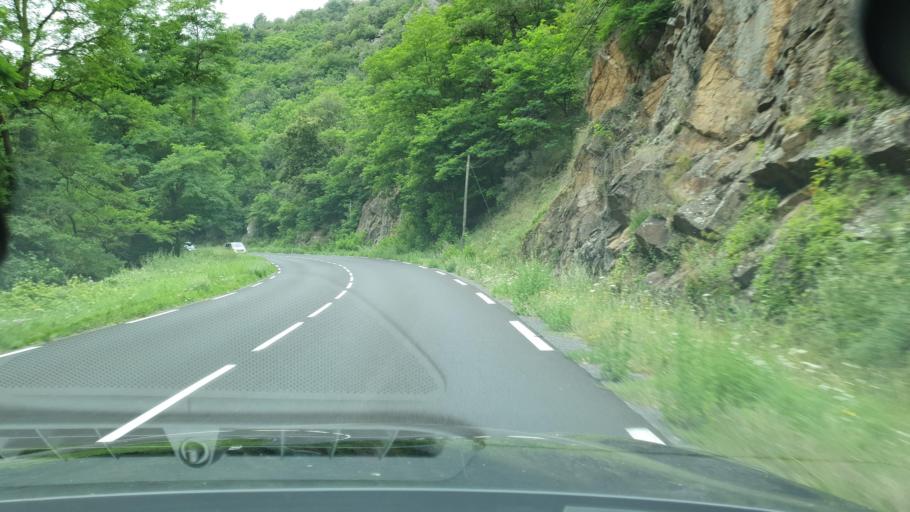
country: FR
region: Auvergne
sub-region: Departement du Puy-de-Dome
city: Champeix
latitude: 45.5774
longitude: 3.0698
